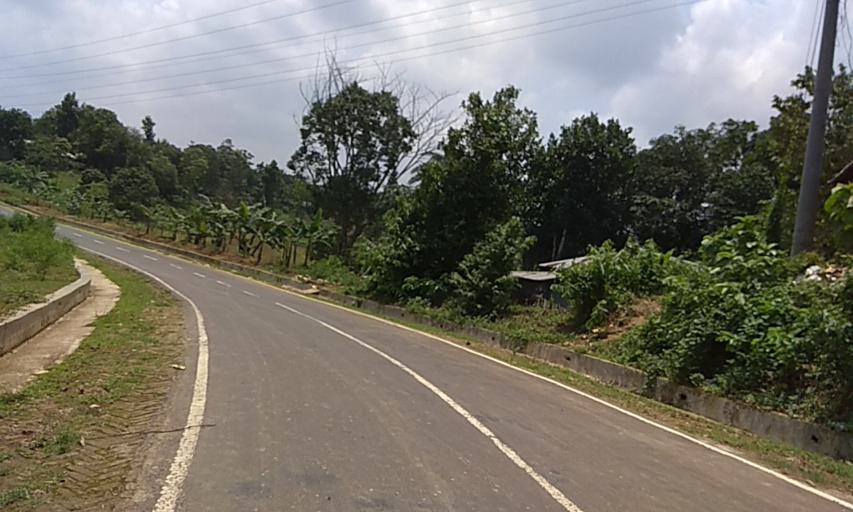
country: BD
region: Chittagong
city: Manikchari
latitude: 22.9354
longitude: 91.8954
